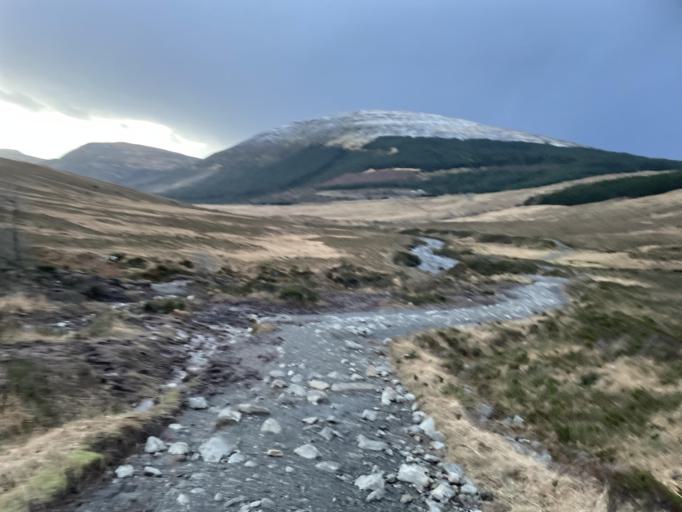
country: GB
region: Scotland
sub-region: Highland
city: Isle of Skye
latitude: 57.2503
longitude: -6.2558
